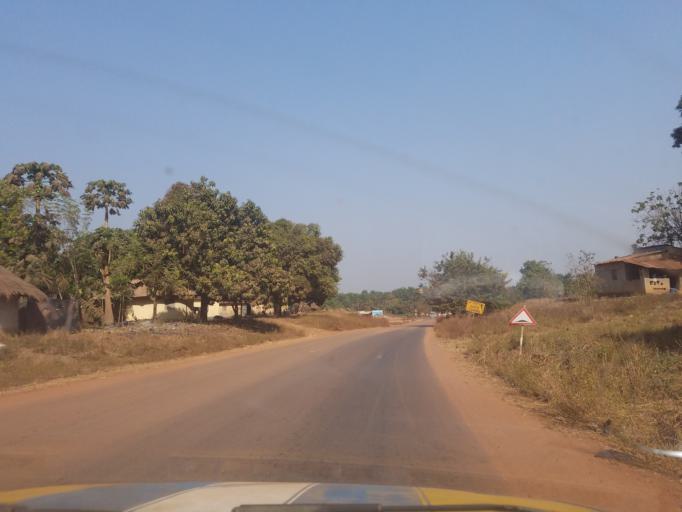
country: GN
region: Boke
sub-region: Boke Prefecture
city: Boke
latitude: 10.8342
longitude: -14.3644
